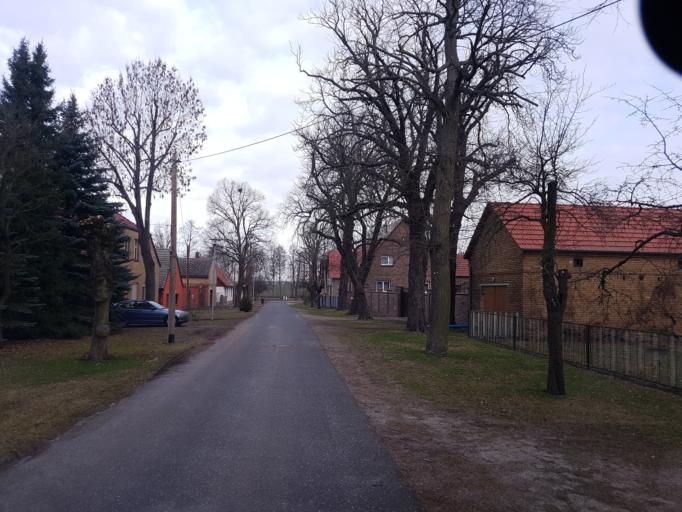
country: DE
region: Brandenburg
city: Finsterwalde
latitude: 51.6173
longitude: 13.7619
